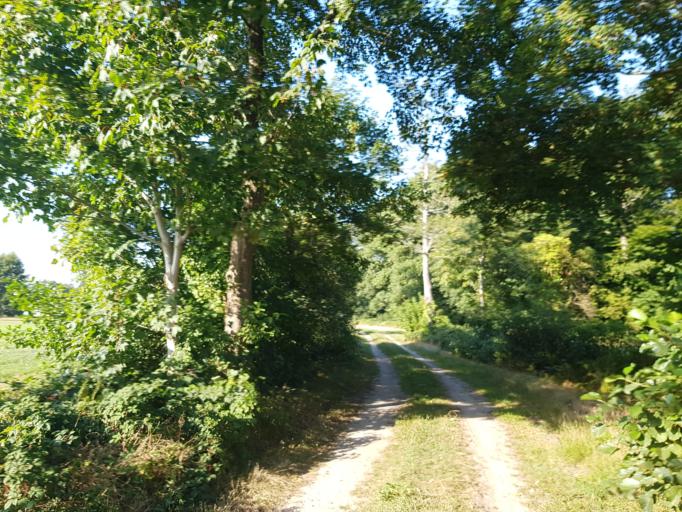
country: NL
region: Drenthe
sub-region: Gemeente Westerveld
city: Dwingeloo
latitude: 52.8221
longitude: 6.3428
